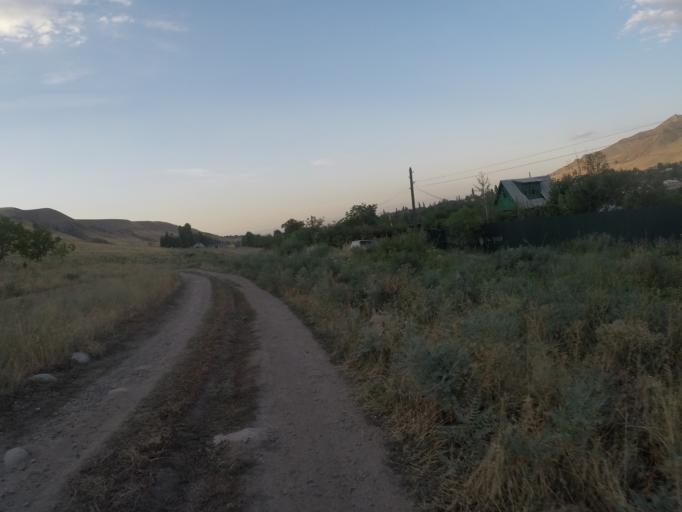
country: KG
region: Chuy
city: Bishkek
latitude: 42.7697
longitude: 74.6389
